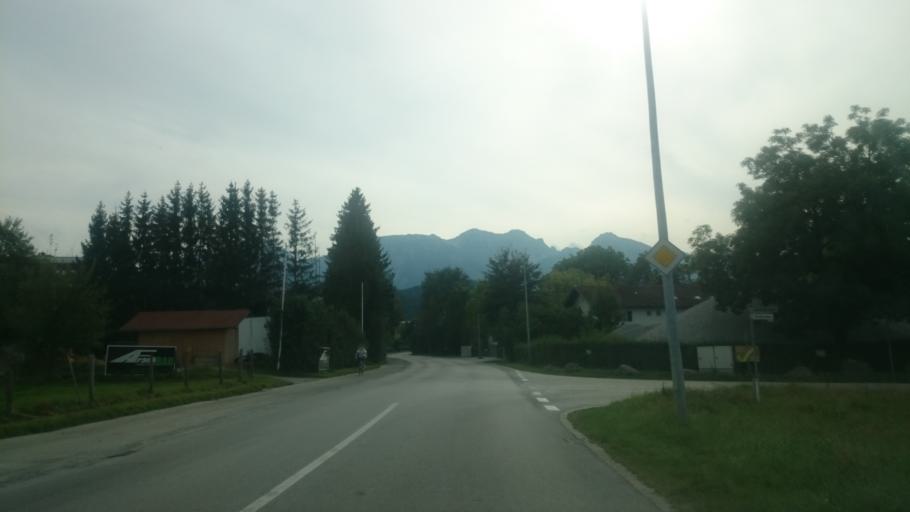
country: DE
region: Bavaria
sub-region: Swabia
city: Fuessen
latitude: 47.5773
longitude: 10.6801
